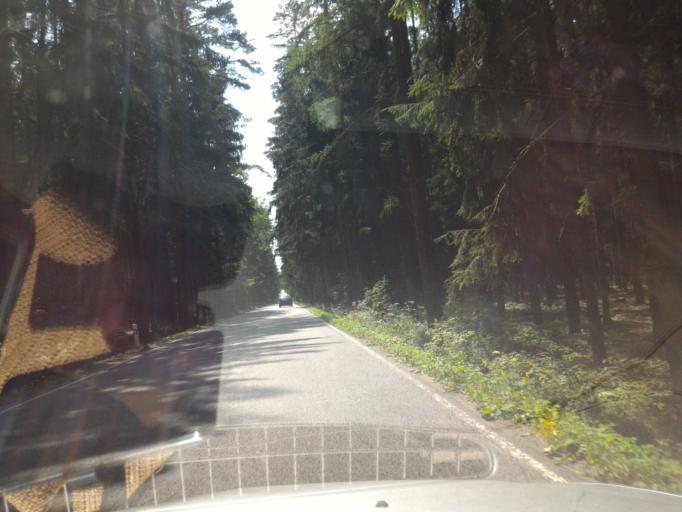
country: CZ
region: Vysocina
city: Velky Beranov
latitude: 49.4274
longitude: 15.7001
